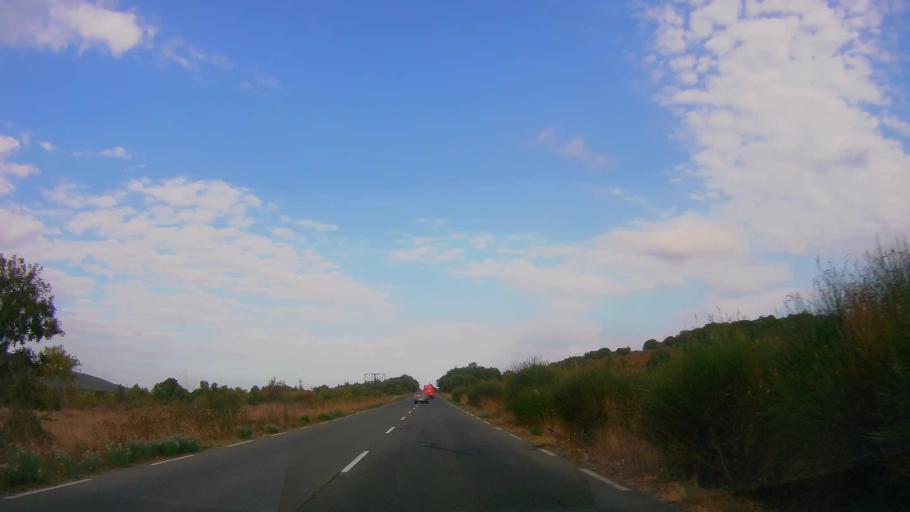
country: BG
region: Burgas
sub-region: Obshtina Sozopol
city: Sozopol
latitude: 42.3666
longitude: 27.6905
